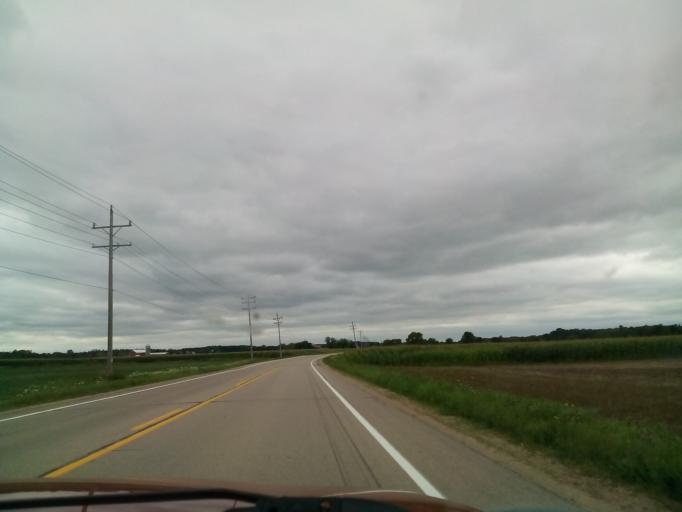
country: US
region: Wisconsin
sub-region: Waupaca County
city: New London
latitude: 44.2672
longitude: -88.7862
